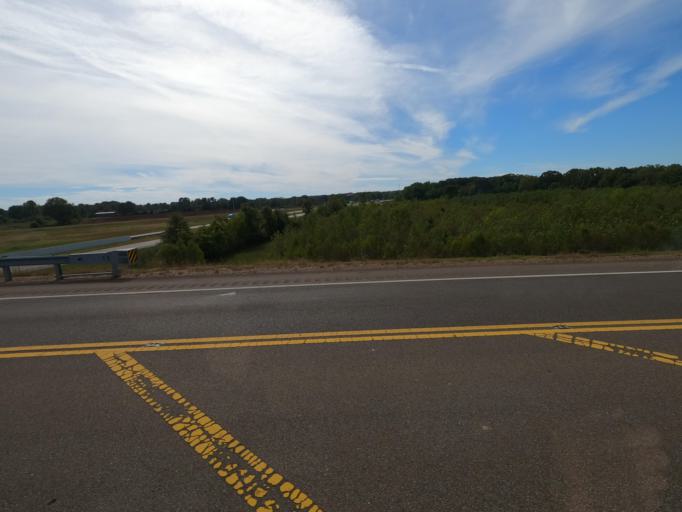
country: US
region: Tennessee
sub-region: Shelby County
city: Arlington
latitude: 35.2923
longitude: -89.6112
